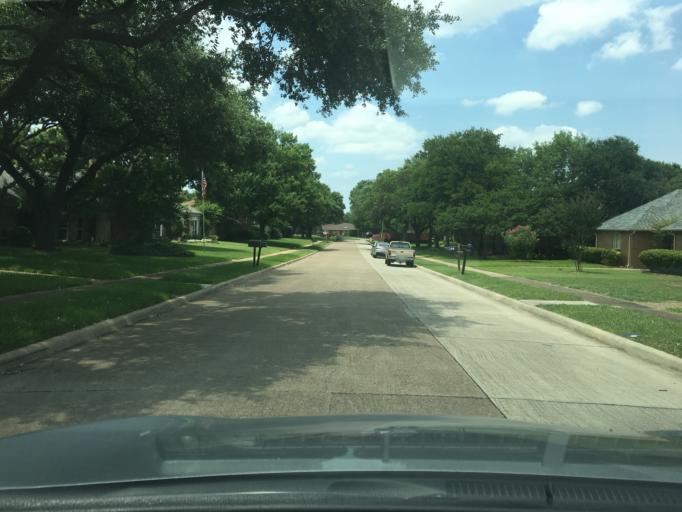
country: US
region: Texas
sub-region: Dallas County
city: Richardson
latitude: 32.9536
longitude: -96.6971
